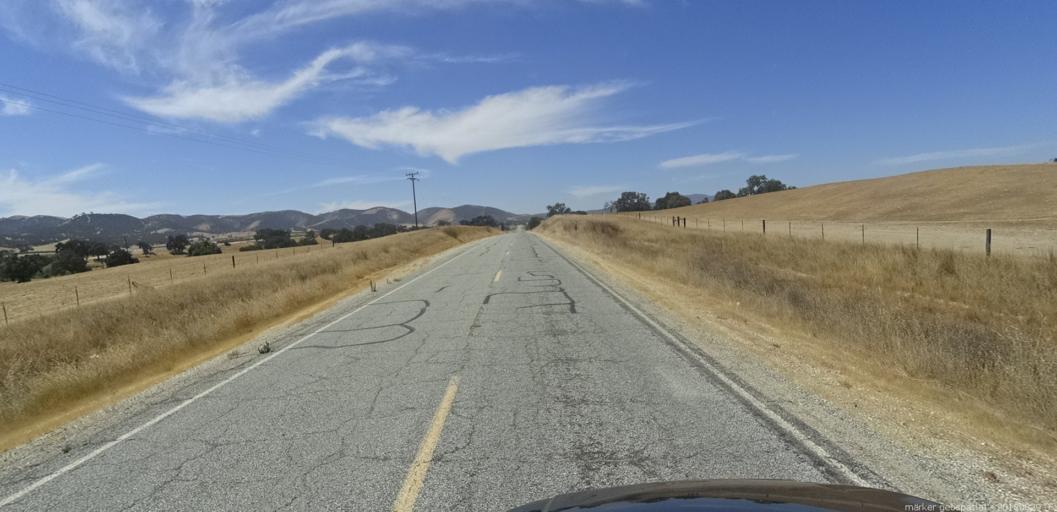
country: US
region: California
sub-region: San Luis Obispo County
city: Lake Nacimiento
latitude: 35.8704
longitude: -120.8639
